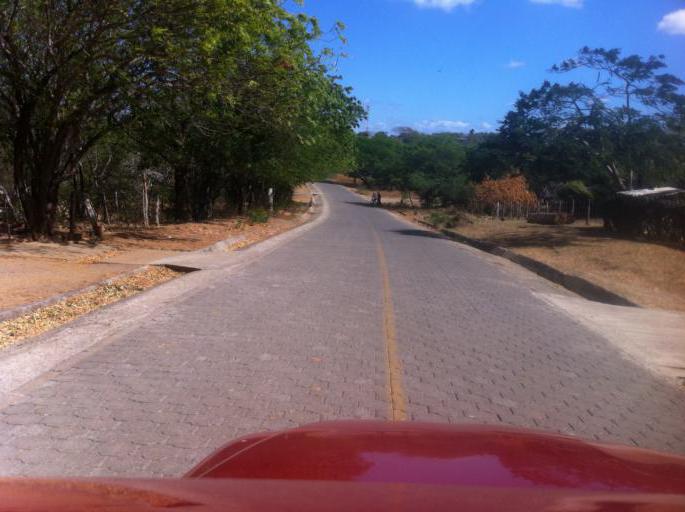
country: NI
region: Carazo
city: El Rosario
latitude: 11.6204
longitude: -86.3282
